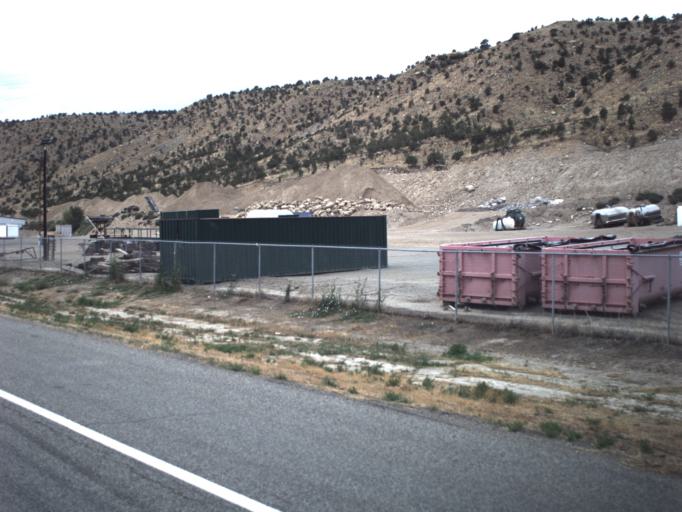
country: US
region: Utah
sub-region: Carbon County
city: Helper
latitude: 39.6800
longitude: -110.8602
